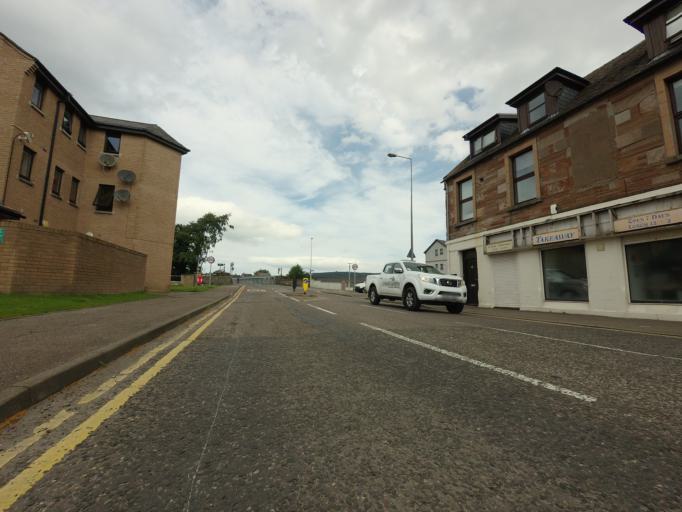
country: GB
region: Scotland
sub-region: Highland
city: Inverness
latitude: 57.4830
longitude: -4.2314
